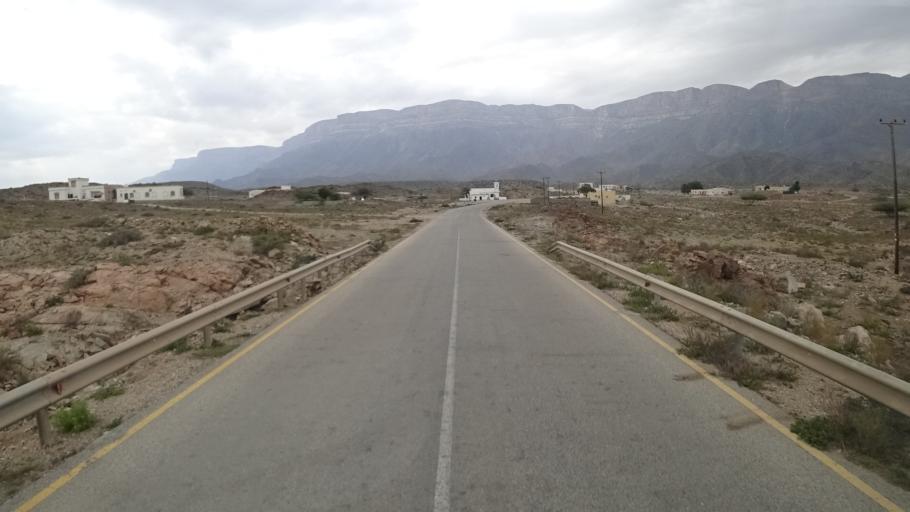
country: OM
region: Zufar
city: Salalah
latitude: 17.1626
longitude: 54.9843
